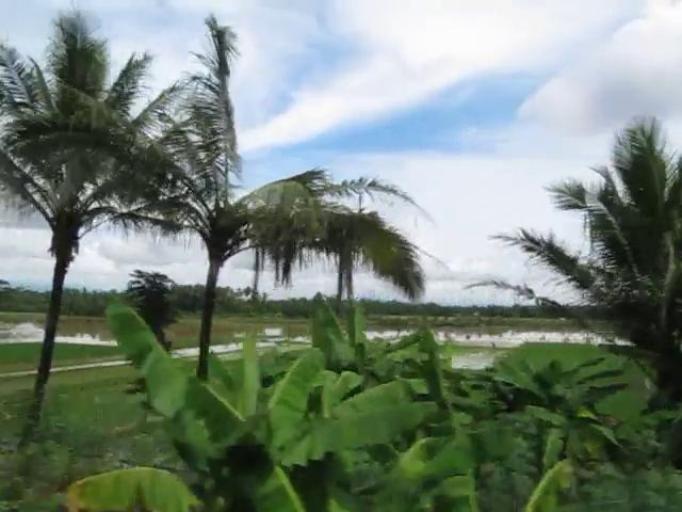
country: ID
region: Central Java
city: Meluwung
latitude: -7.3897
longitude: 108.6968
